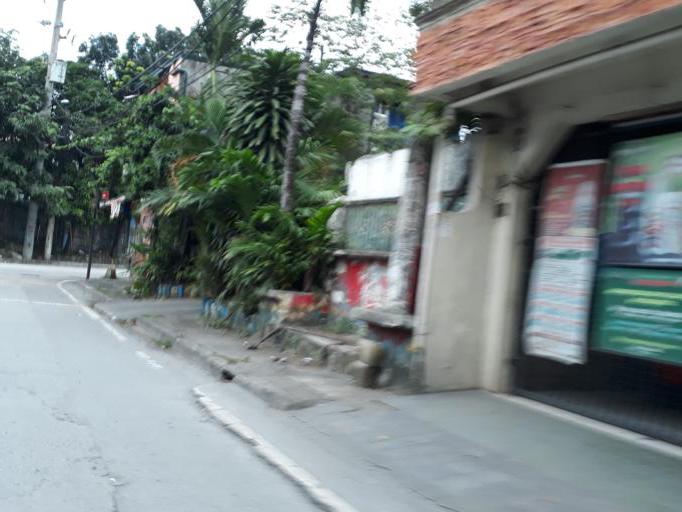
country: PH
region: Calabarzon
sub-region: Province of Rizal
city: Valenzuela
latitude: 14.6978
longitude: 120.9965
